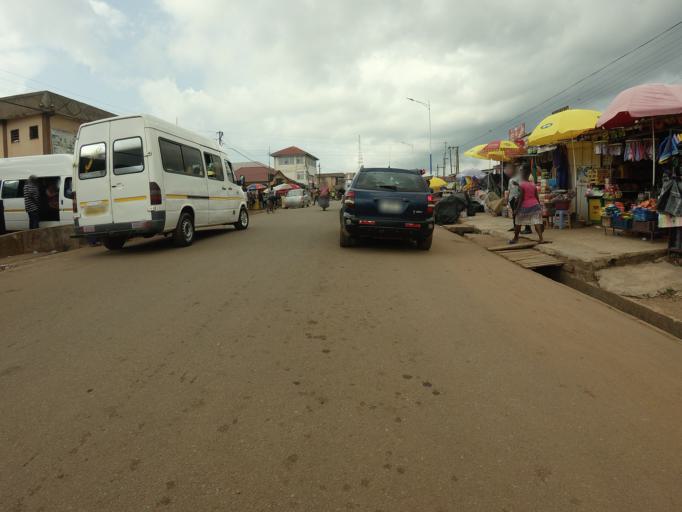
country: GH
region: Volta
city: Hohoe
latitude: 7.1501
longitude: 0.4696
